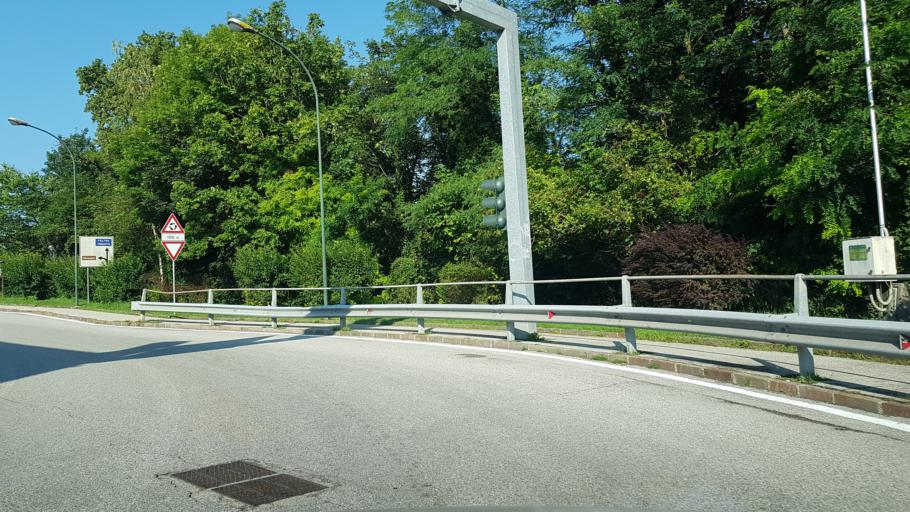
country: IT
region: Veneto
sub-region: Provincia di Belluno
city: Belluno
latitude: 46.1340
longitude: 12.2183
